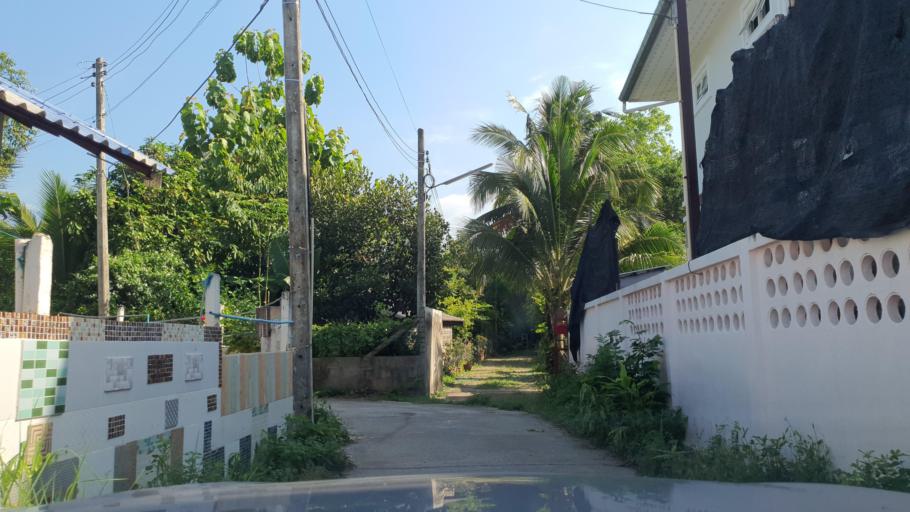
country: TH
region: Chiang Mai
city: Hang Dong
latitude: 18.7222
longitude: 98.9329
